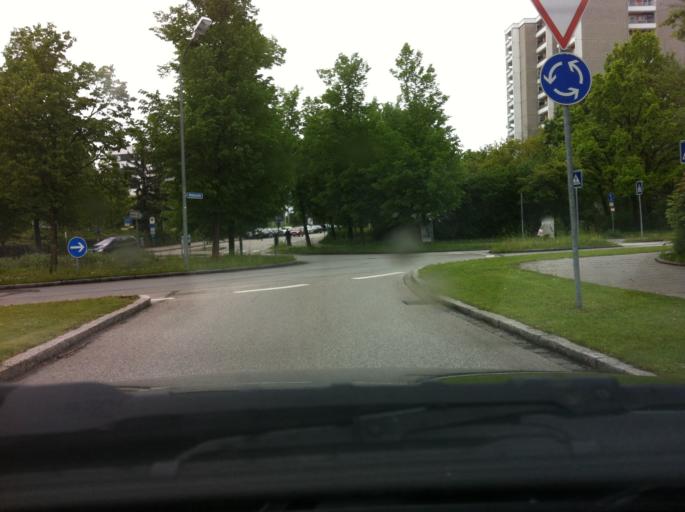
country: DE
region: Bavaria
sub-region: Upper Bavaria
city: Taufkirchen
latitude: 48.0549
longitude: 11.6068
